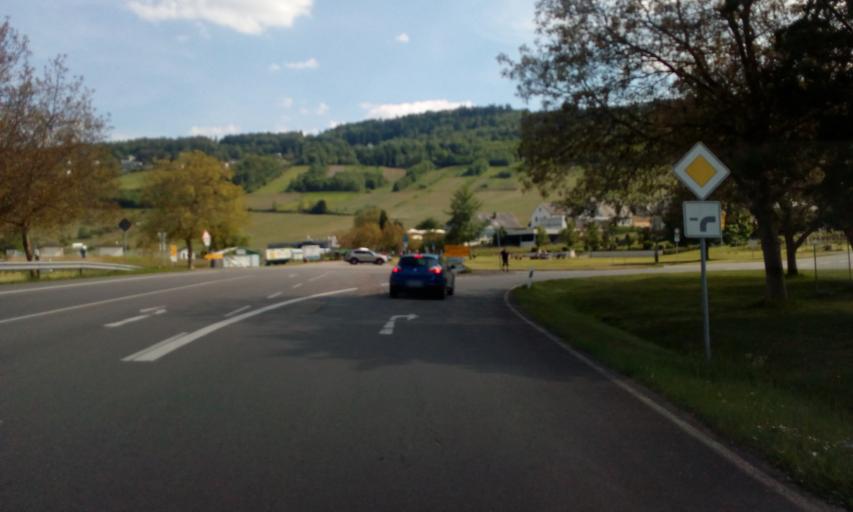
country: DE
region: Rheinland-Pfalz
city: Leiwen
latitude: 49.8189
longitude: 6.8859
